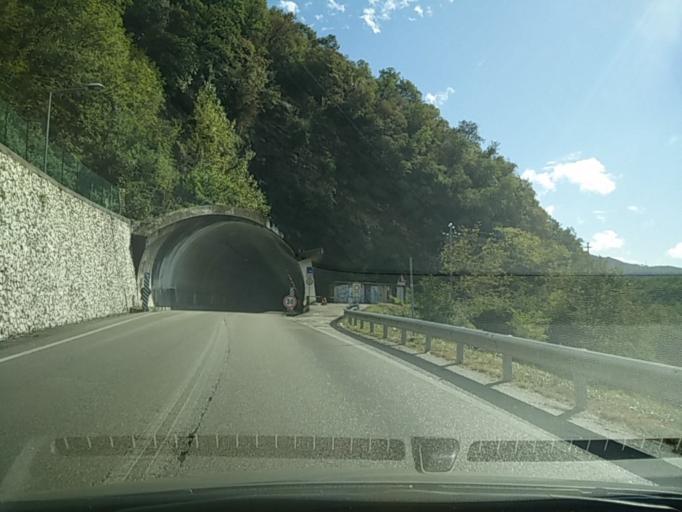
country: IT
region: Veneto
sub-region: Provincia di Belluno
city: Vas
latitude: 45.9307
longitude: 11.9420
